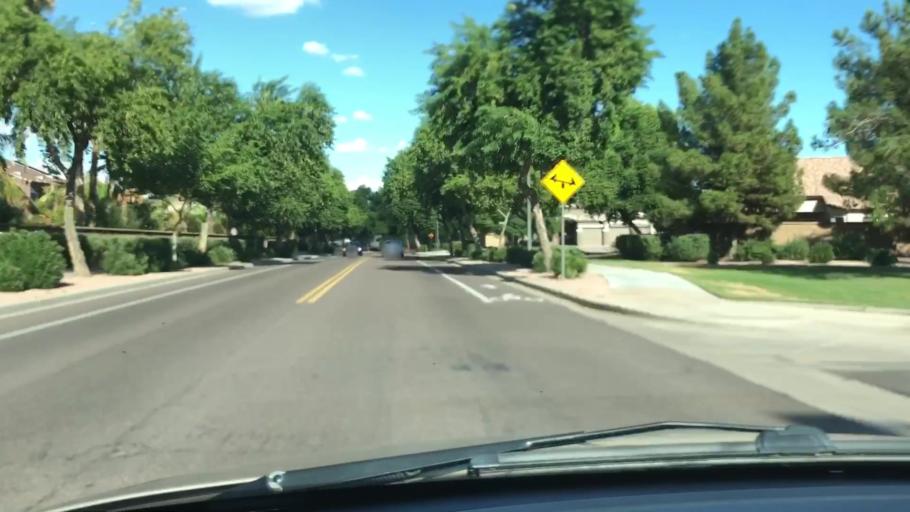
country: US
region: Arizona
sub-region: Maricopa County
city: Queen Creek
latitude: 33.2667
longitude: -111.7176
